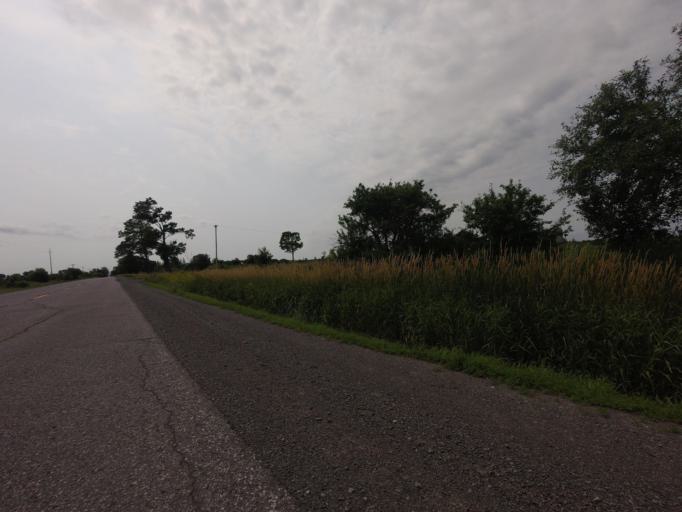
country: CA
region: Ontario
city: Arnprior
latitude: 45.3788
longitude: -76.1719
